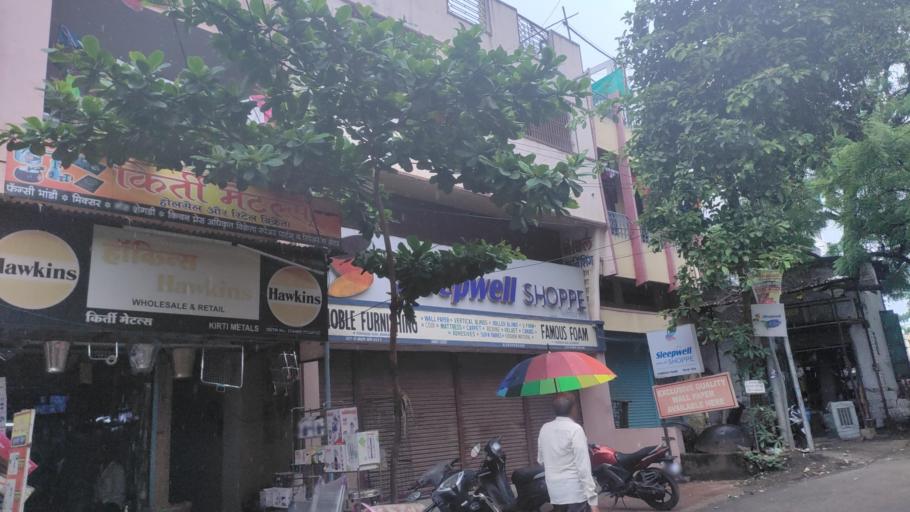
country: IN
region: Maharashtra
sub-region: Aurangabad Division
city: Aurangabad
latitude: 19.8864
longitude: 75.3326
